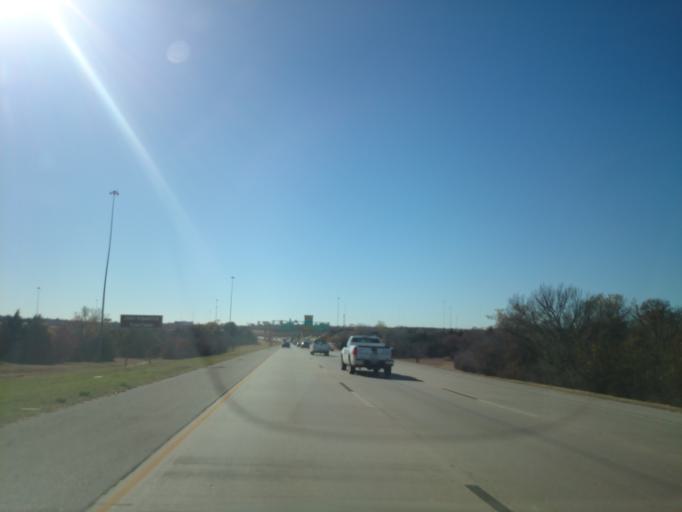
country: US
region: Oklahoma
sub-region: Oklahoma County
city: Edmond
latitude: 35.6059
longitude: -97.4271
